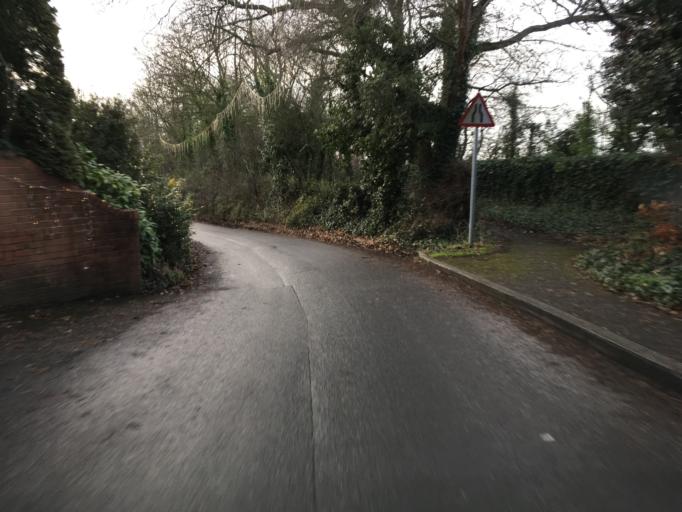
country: GB
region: England
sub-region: South Gloucestershire
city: Almondsbury
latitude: 51.5565
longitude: -2.5660
